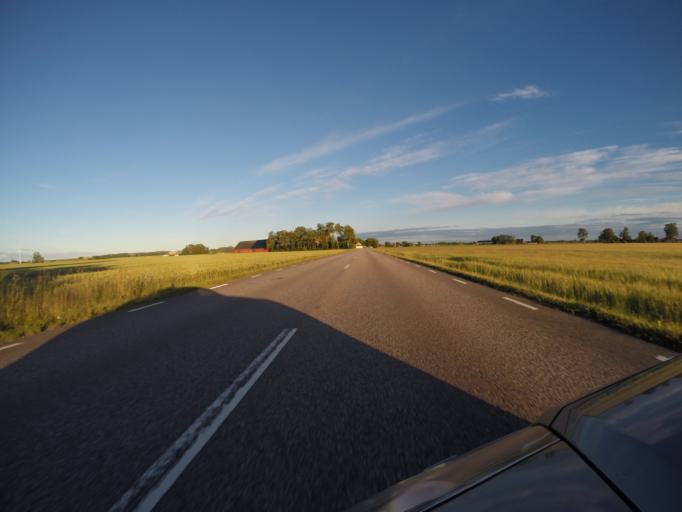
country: SE
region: Skane
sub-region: Helsingborg
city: Hyllinge
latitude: 56.1462
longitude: 12.8706
